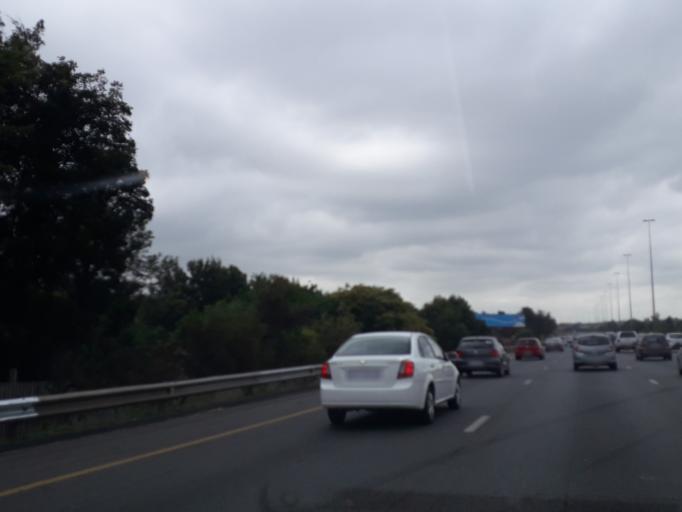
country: ZA
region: Gauteng
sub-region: City of Johannesburg Metropolitan Municipality
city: Roodepoort
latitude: -26.1027
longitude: 27.9629
